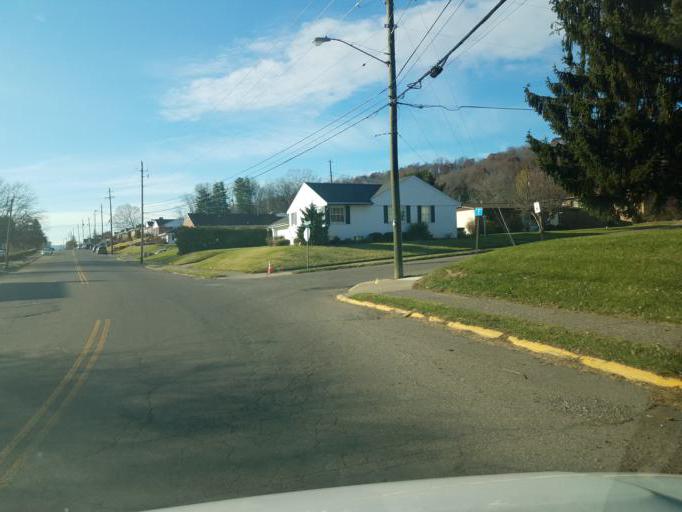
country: US
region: Ohio
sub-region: Scioto County
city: Rosemount
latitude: 38.7587
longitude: -82.9780
